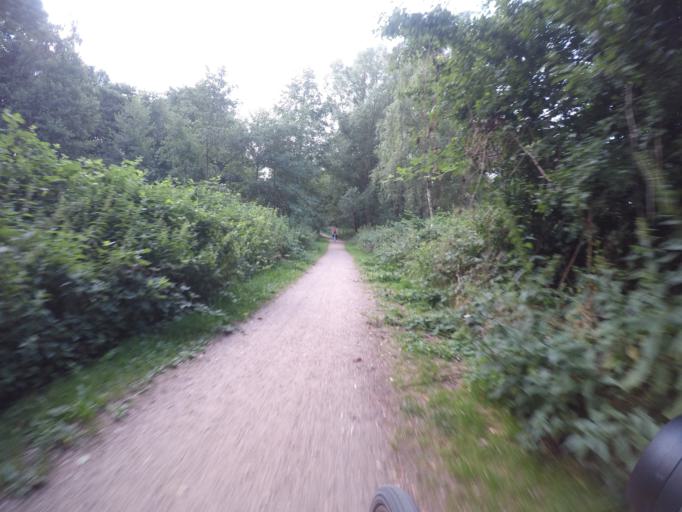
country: DE
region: Schleswig-Holstein
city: Oststeinbek
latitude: 53.5068
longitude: 10.1328
